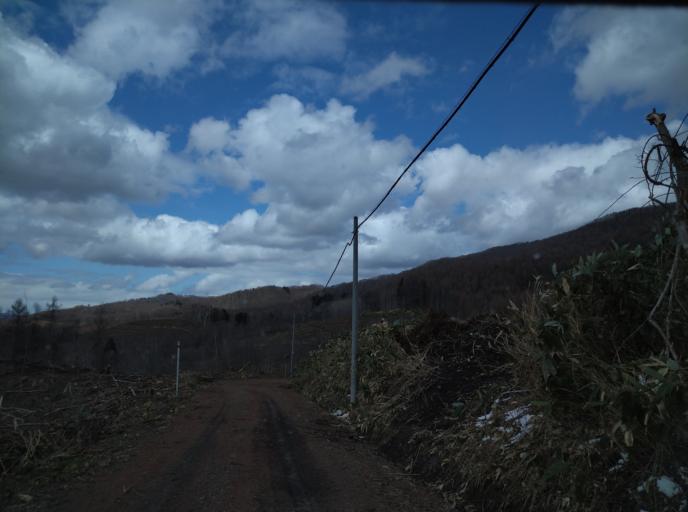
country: JP
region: Hokkaido
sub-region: Asahikawa-shi
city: Asahikawa
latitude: 44.0215
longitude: 142.4375
